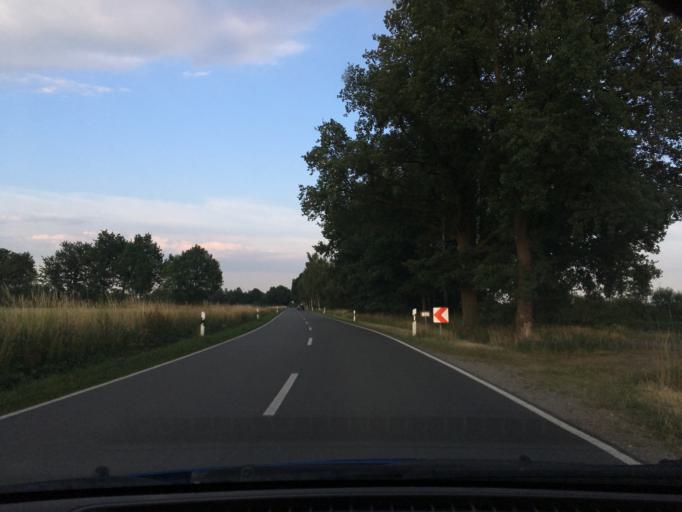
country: DE
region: Lower Saxony
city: Eschede
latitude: 52.7266
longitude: 10.2516
